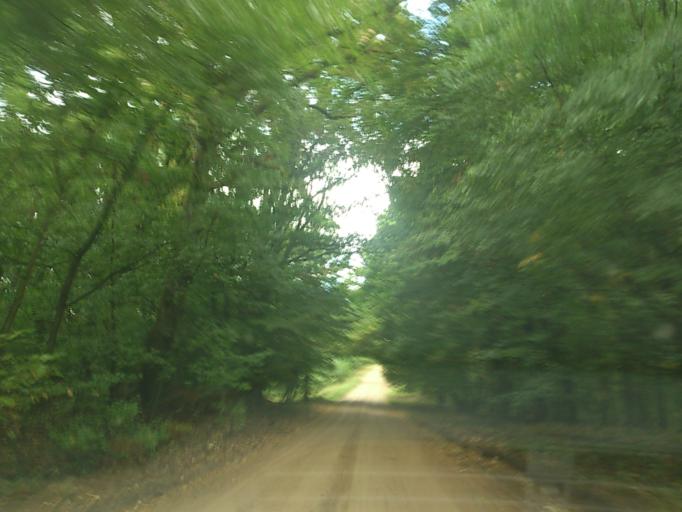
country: PL
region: Greater Poland Voivodeship
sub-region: Powiat poznanski
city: Kobylnica
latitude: 52.5374
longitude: 17.1153
